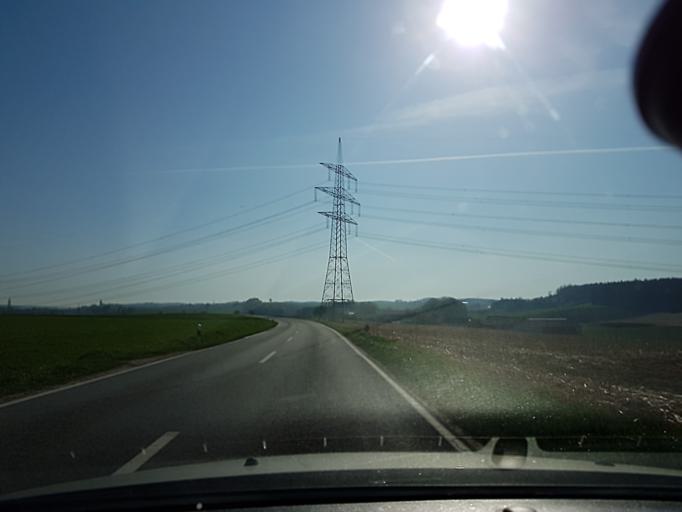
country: DE
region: Bavaria
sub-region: Lower Bavaria
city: Geisenhausen
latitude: 48.4617
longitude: 12.2268
